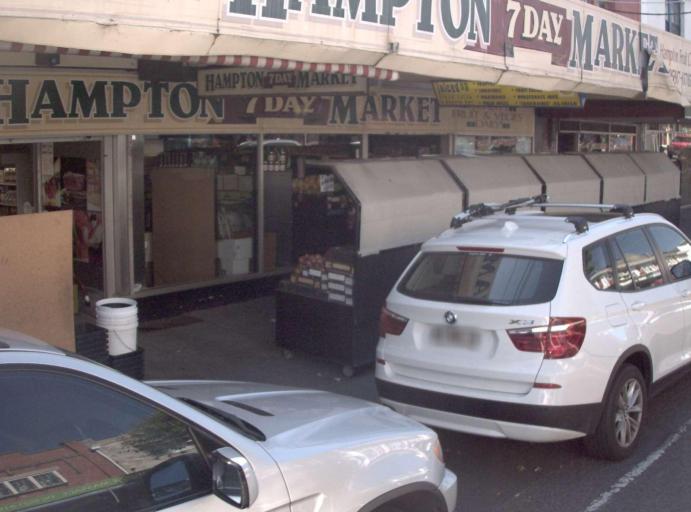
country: AU
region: Victoria
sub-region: Bayside
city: Hampton
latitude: -37.9380
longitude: 145.0024
